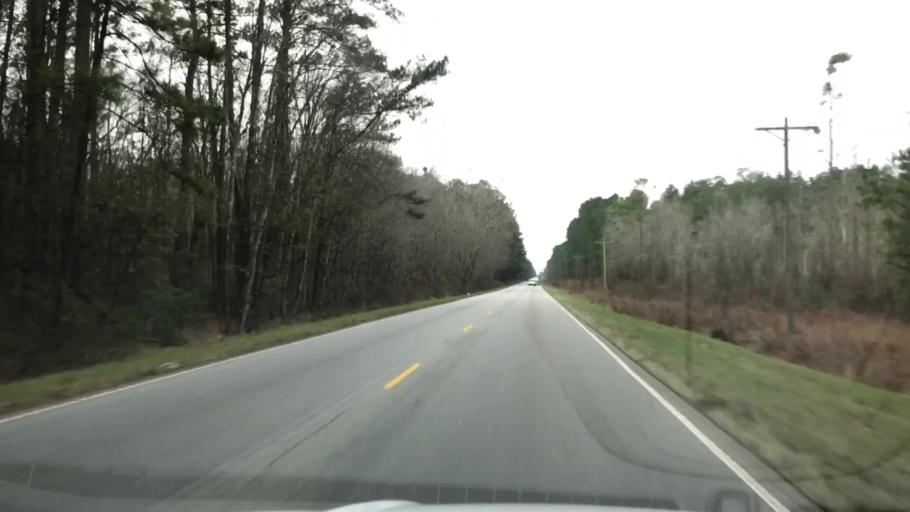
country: US
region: South Carolina
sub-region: Jasper County
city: Ridgeland
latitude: 32.3727
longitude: -80.9144
